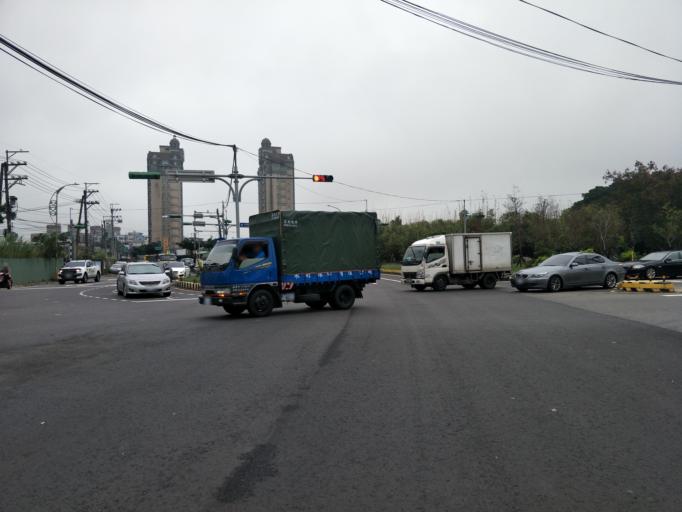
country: TW
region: Taiwan
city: Daxi
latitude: 24.8895
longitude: 121.2702
